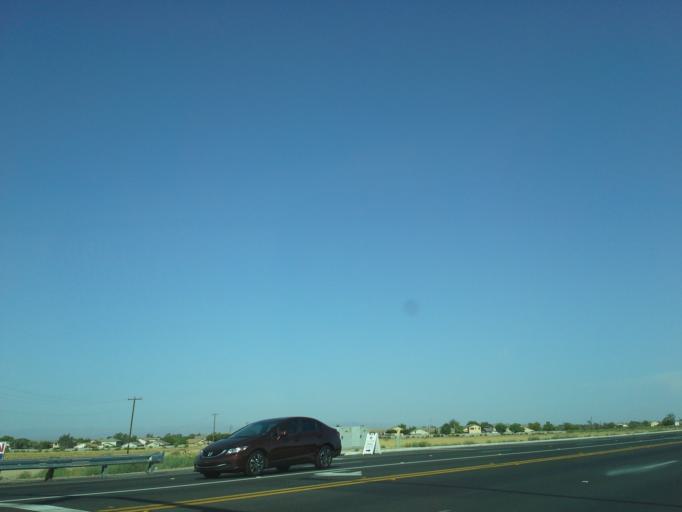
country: US
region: Arizona
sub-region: Maricopa County
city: Queen Creek
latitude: 33.1905
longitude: -111.5999
